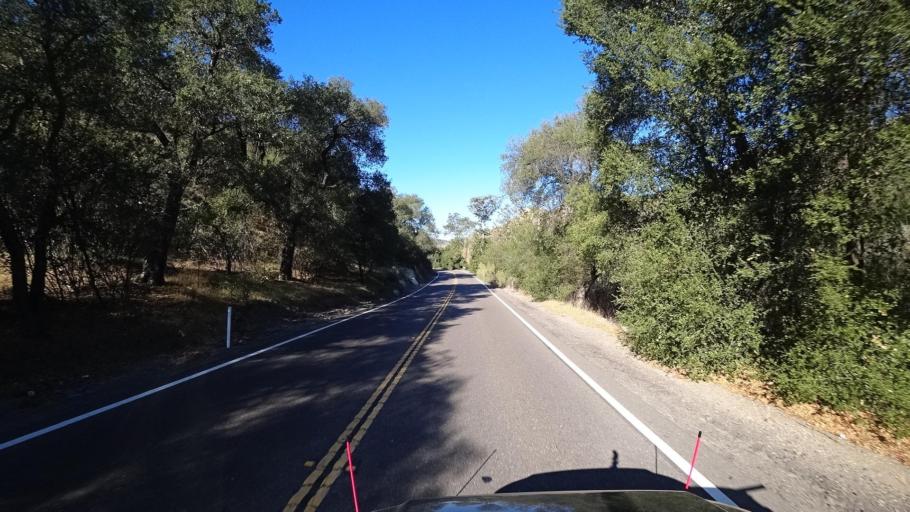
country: US
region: California
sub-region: San Diego County
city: Jamul
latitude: 32.6544
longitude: -116.7950
